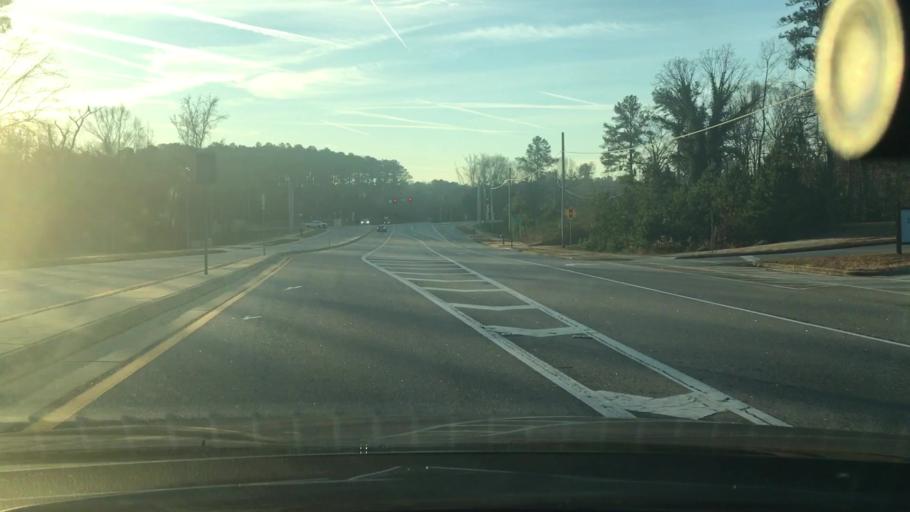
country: US
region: Georgia
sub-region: Coweta County
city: Senoia
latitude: 33.3286
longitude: -84.5133
